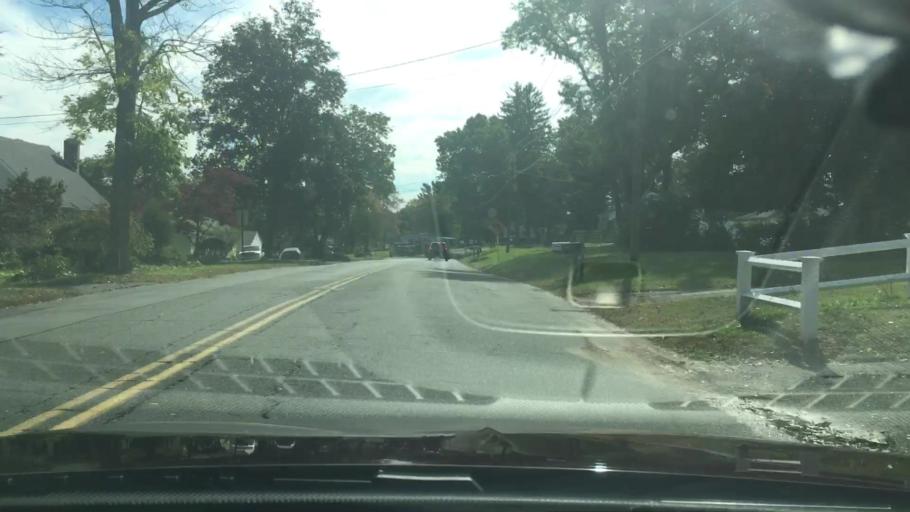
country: US
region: Connecticut
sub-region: Hartford County
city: Plainville
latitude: 41.6508
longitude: -72.8833
